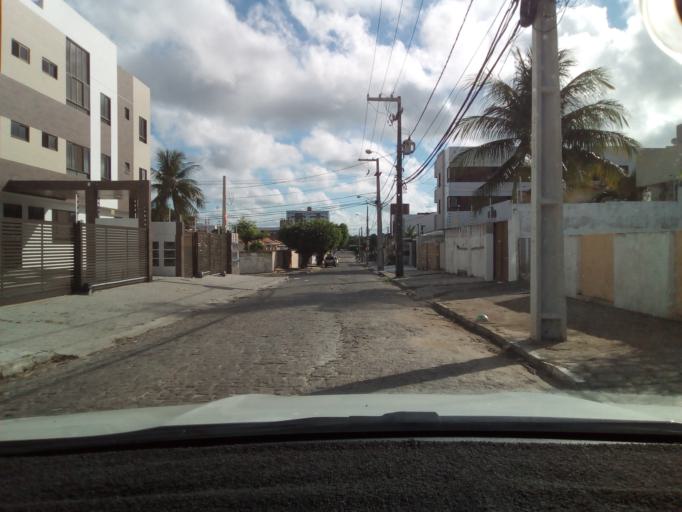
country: BR
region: Paraiba
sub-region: Joao Pessoa
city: Joao Pessoa
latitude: -7.1360
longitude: -34.8287
